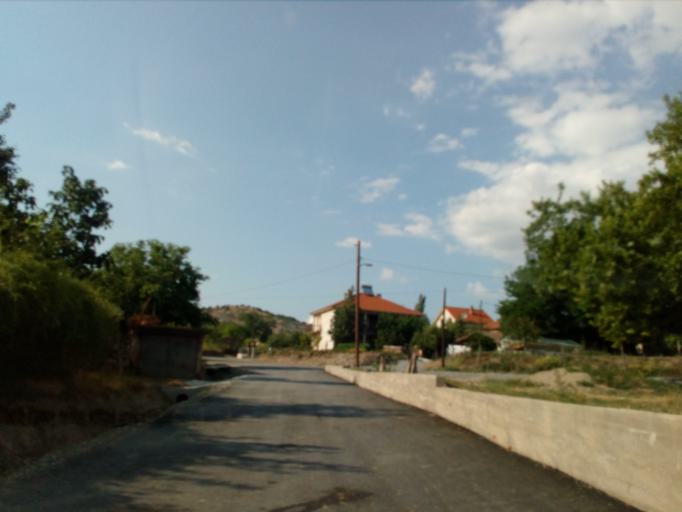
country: MK
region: Veles
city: Veles
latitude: 41.7543
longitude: 21.7965
